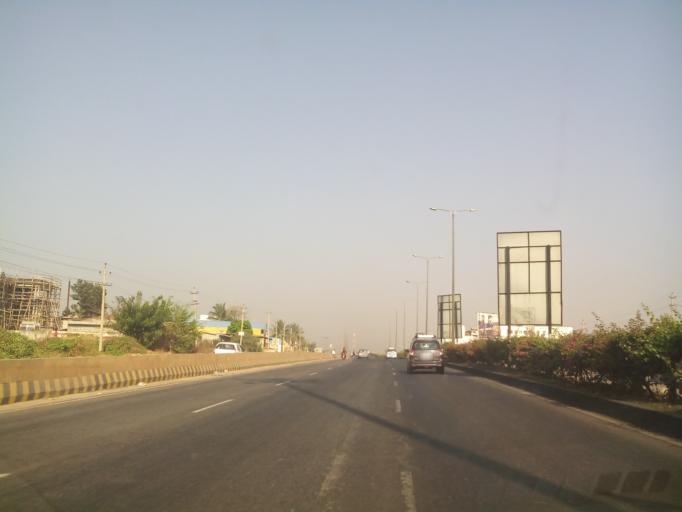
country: IN
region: Karnataka
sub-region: Bangalore Rural
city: Nelamangala
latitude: 13.0911
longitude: 77.3990
